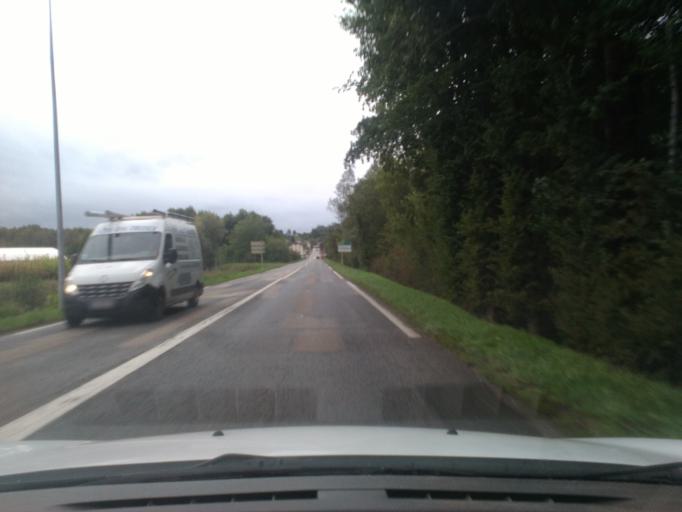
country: FR
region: Lorraine
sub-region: Departement des Vosges
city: Saint-Michel-sur-Meurthe
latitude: 48.3253
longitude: 6.8955
